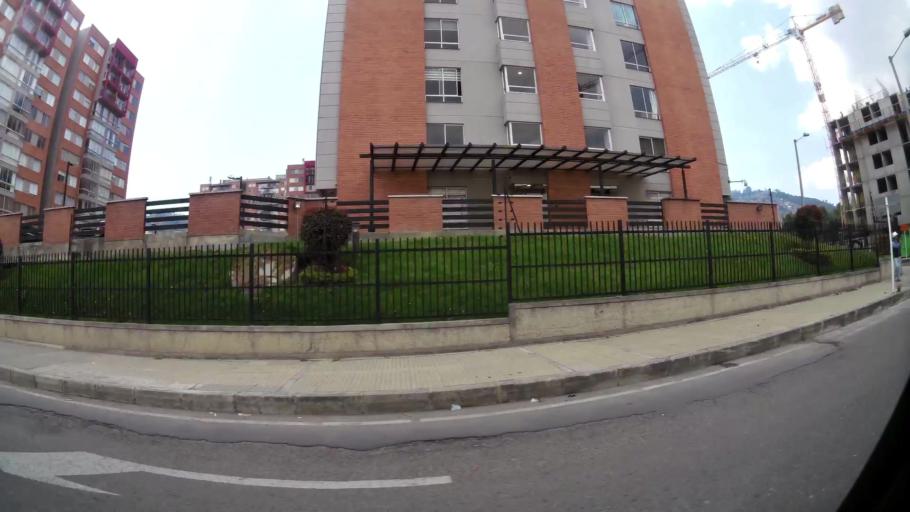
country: CO
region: Cundinamarca
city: La Calera
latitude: 4.7454
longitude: -74.0269
